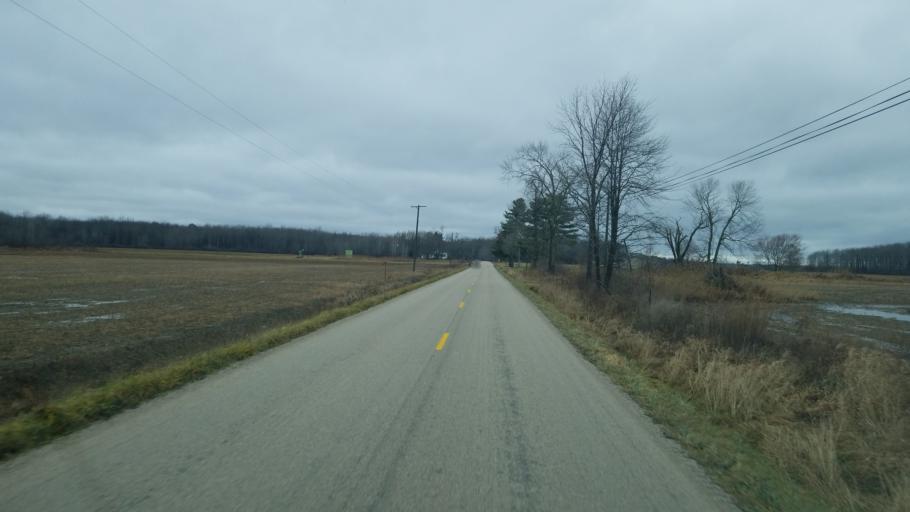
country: US
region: Ohio
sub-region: Ashtabula County
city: Andover
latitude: 41.6877
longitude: -80.6137
